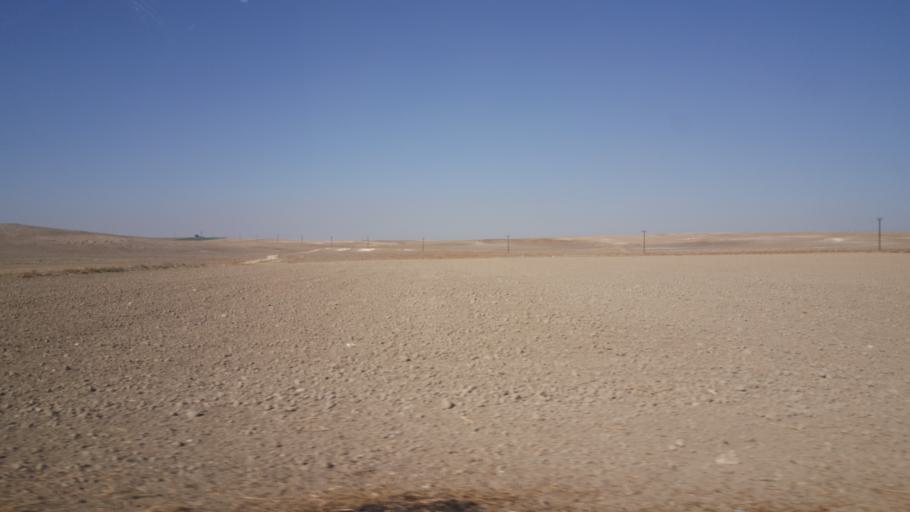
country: TR
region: Konya
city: Celtik
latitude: 39.0612
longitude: 31.8580
